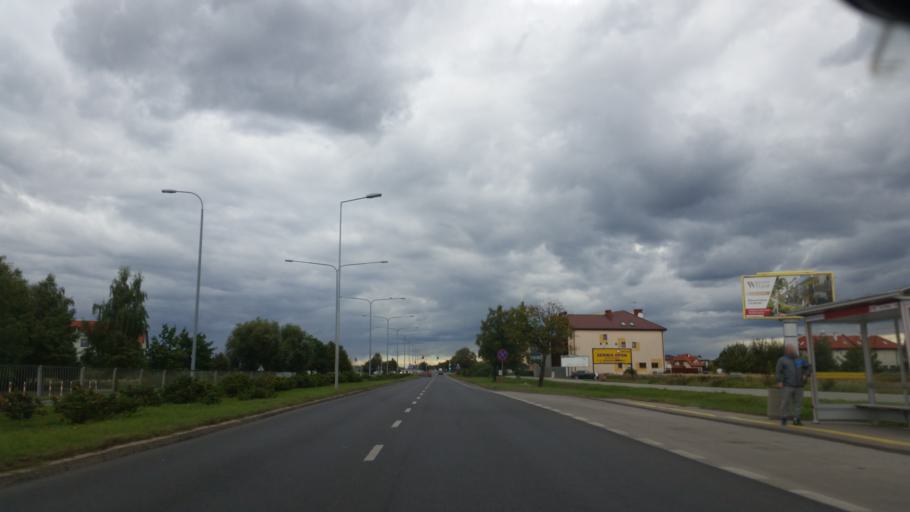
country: PL
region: Masovian Voivodeship
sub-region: Warszawa
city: Kabaty
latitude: 52.1281
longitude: 21.0972
